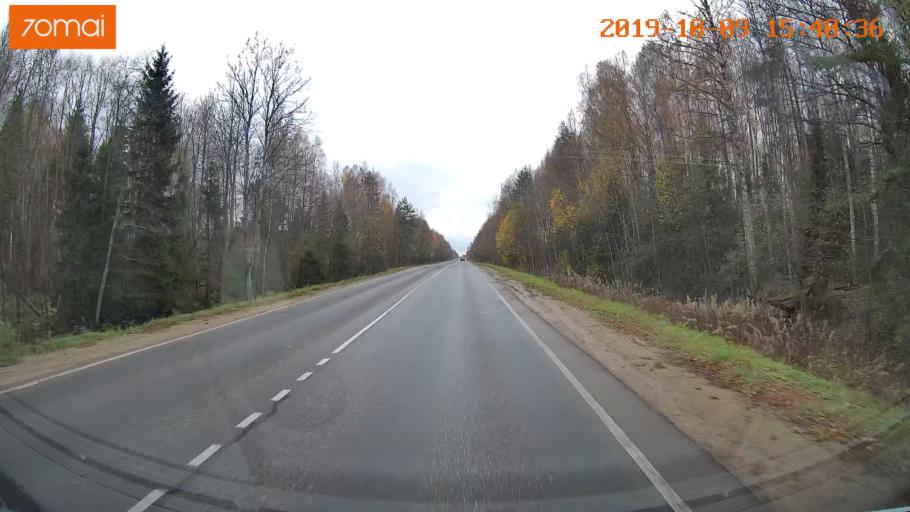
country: RU
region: Kostroma
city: Oktyabr'skiy
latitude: 57.8861
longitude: 41.1412
